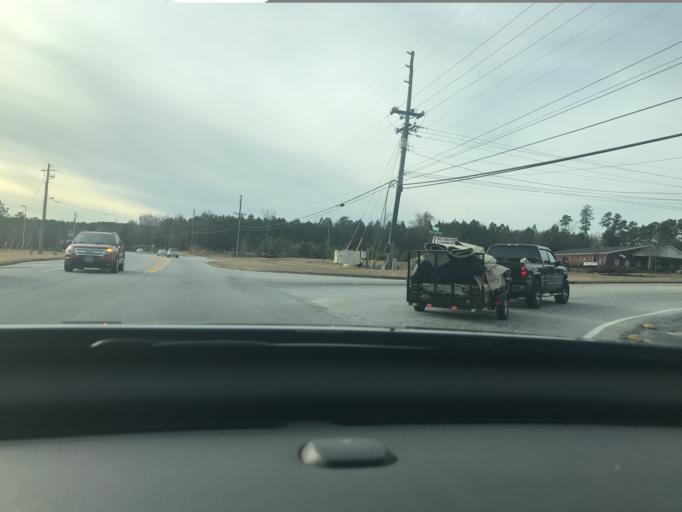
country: US
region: Georgia
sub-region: Newton County
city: Porterdale
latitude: 33.5843
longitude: -83.9134
